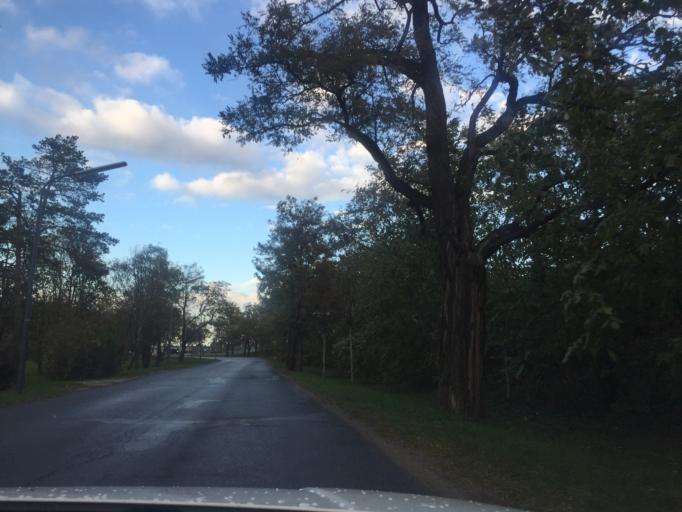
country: AT
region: Lower Austria
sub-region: Politischer Bezirk Wien-Umgebung
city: Gerasdorf bei Wien
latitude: 48.2803
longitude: 16.4603
